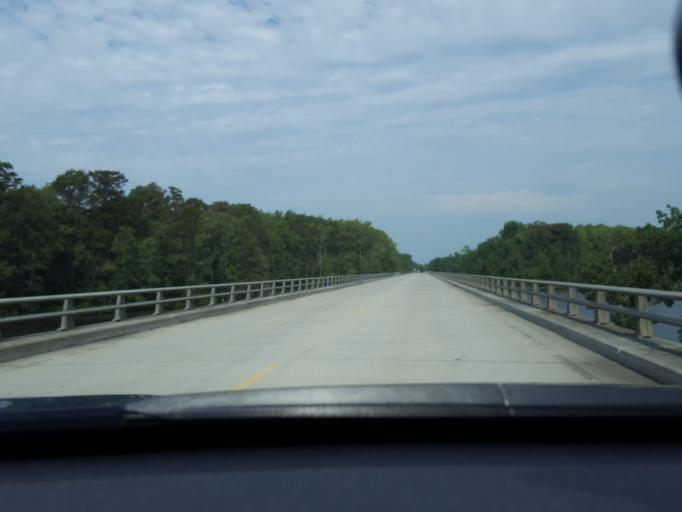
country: US
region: North Carolina
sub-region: Washington County
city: Plymouth
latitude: 35.9197
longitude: -76.7285
